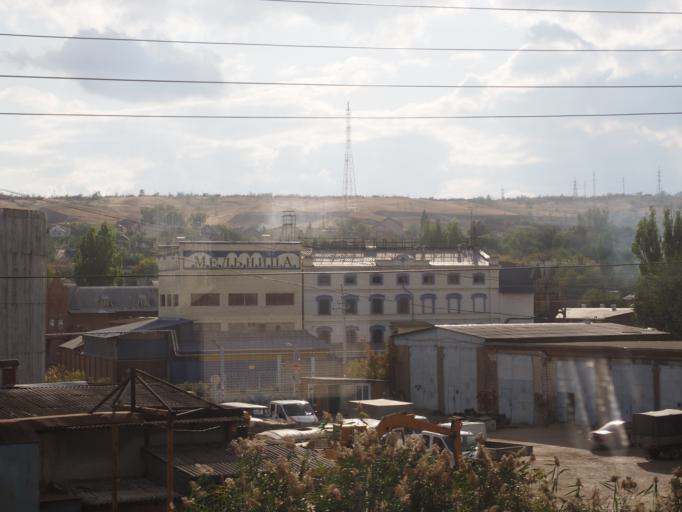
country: RU
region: Volgograd
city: Krasnoslobodsk
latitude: 48.5070
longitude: 44.5465
